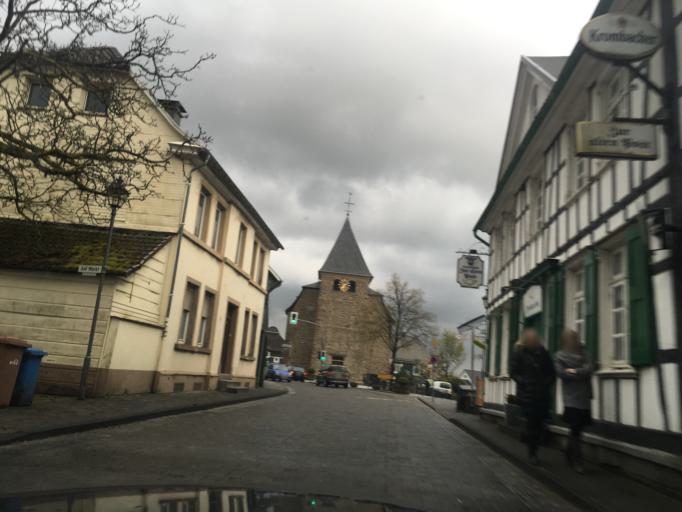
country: DE
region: North Rhine-Westphalia
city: Burscheid
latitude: 51.1154
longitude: 7.1095
